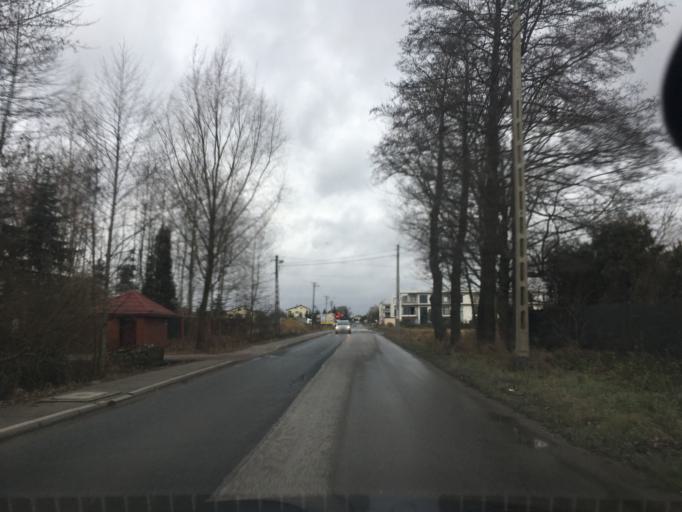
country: PL
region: Masovian Voivodeship
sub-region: Powiat piaseczynski
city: Lesznowola
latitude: 52.1004
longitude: 20.9325
